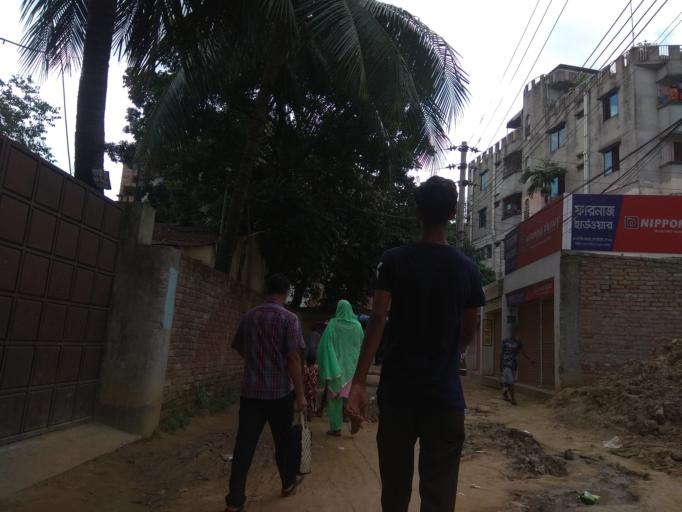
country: BD
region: Dhaka
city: Tungi
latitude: 23.8132
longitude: 90.3881
